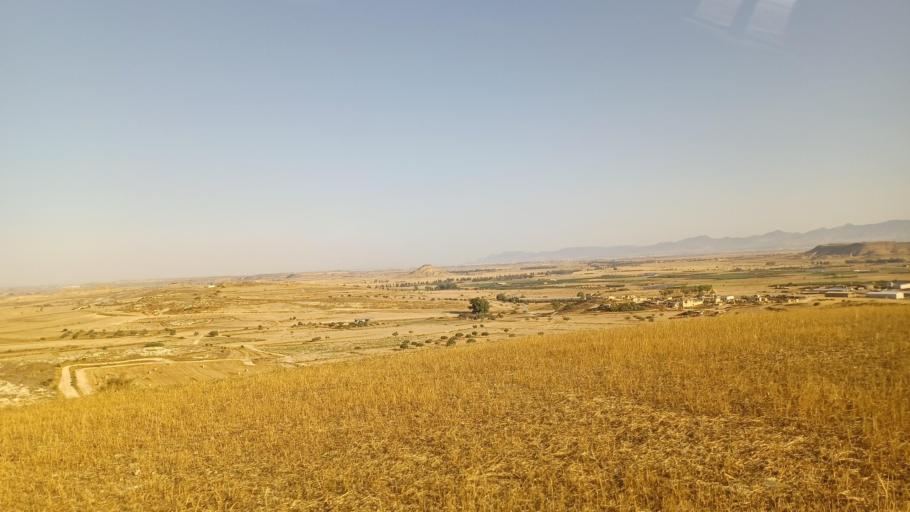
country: CY
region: Larnaka
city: Athienou
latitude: 35.0399
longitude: 33.5242
